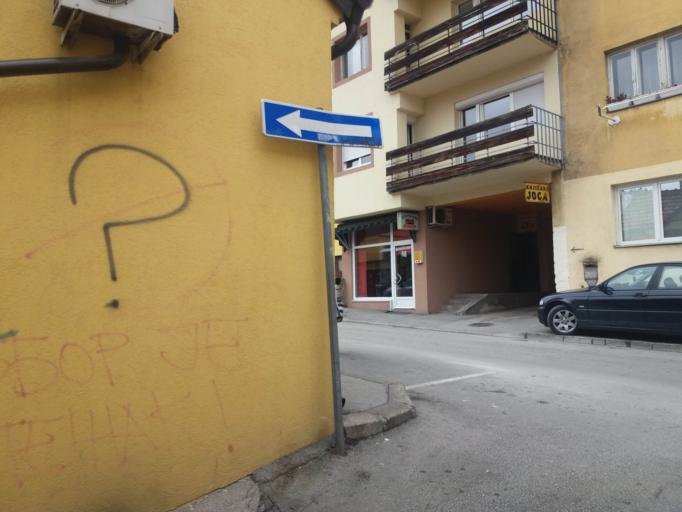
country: RS
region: Central Serbia
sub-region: Zlatiborski Okrug
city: Uzice
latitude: 43.8594
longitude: 19.8410
